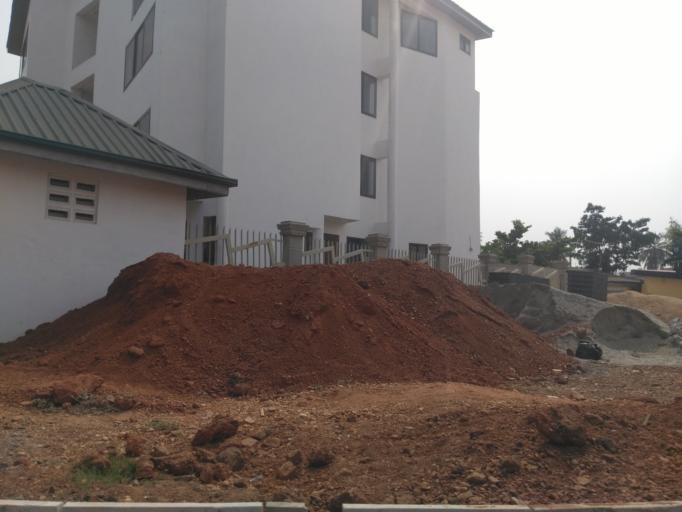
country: GH
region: Greater Accra
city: Accra
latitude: 5.5627
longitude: -0.1784
